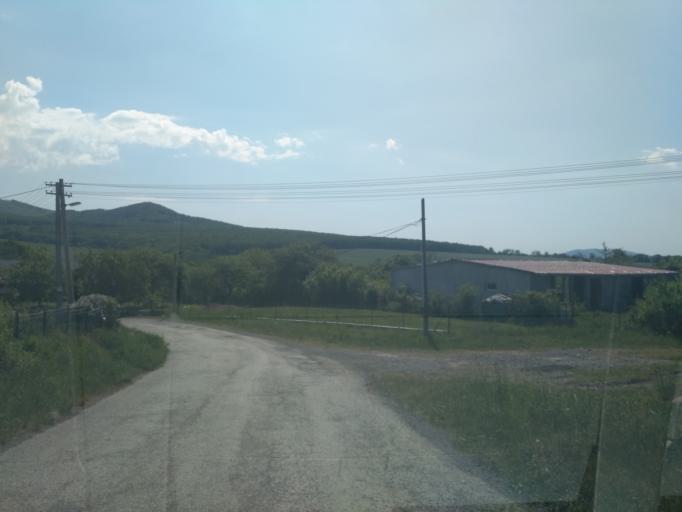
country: SK
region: Kosicky
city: Kosice
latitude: 48.8467
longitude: 21.4339
